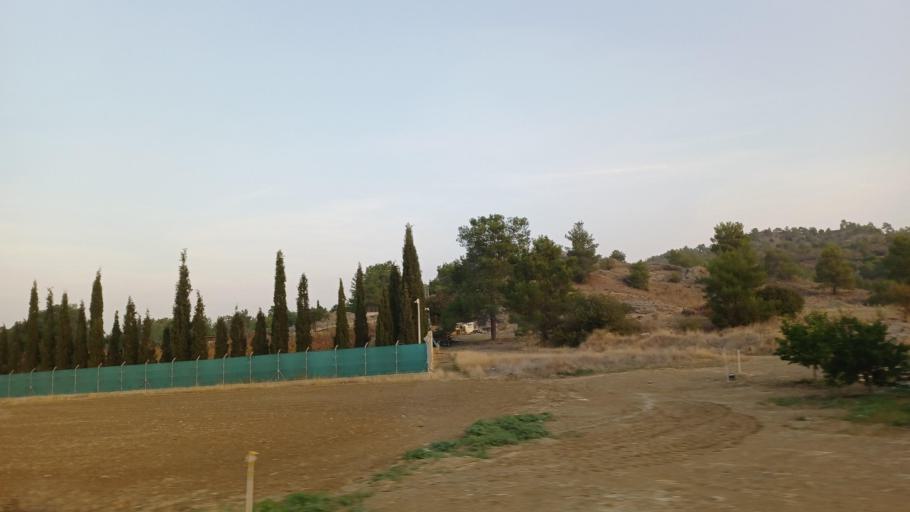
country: CY
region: Larnaka
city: Kornos
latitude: 34.9139
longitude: 33.3679
